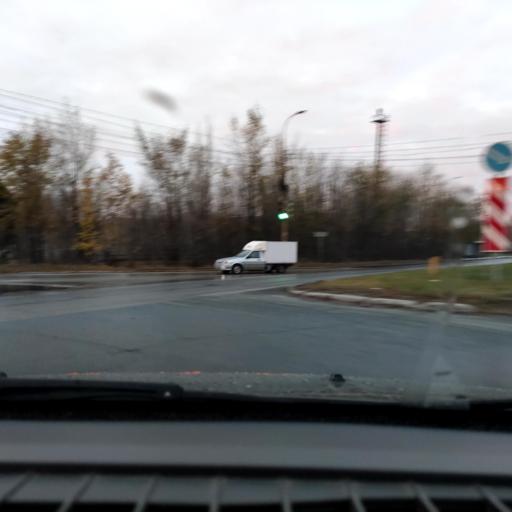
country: RU
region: Samara
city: Tol'yatti
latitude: 53.5586
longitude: 49.3198
